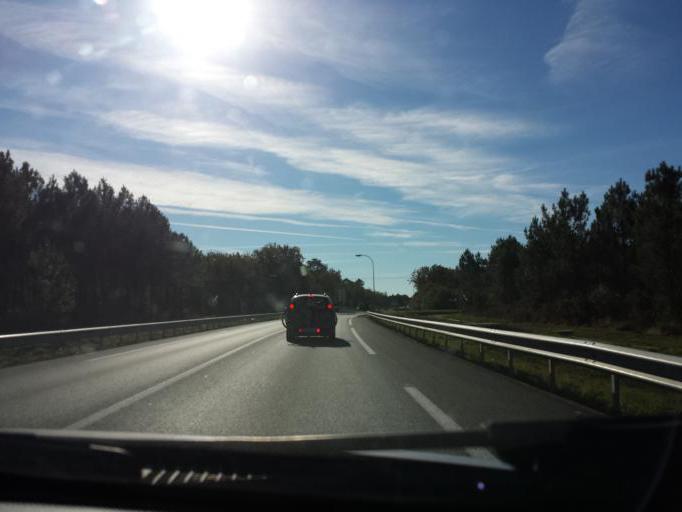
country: FR
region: Aquitaine
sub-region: Departement de la Gironde
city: Lacanau
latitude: 44.9811
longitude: -1.0630
